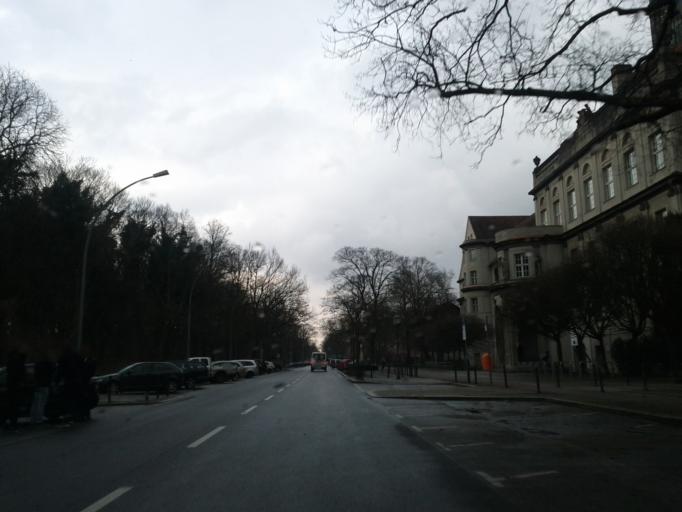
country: DE
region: Berlin
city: Plaenterwald
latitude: 52.4841
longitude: 13.4797
